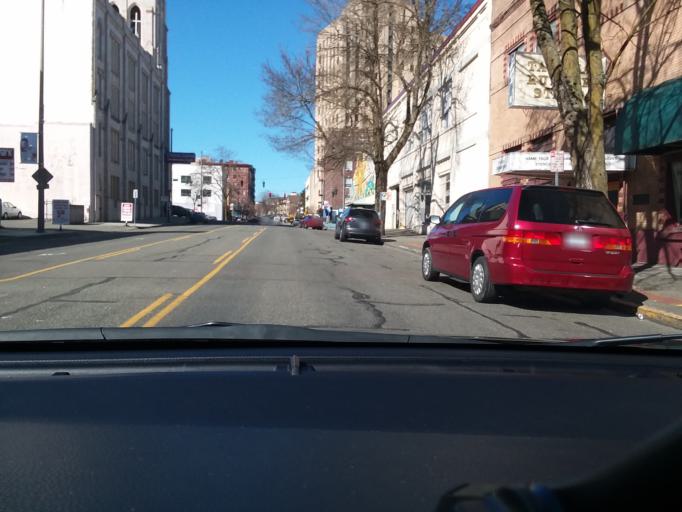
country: US
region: Washington
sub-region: Pierce County
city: Tacoma
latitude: 47.2543
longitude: -122.4418
